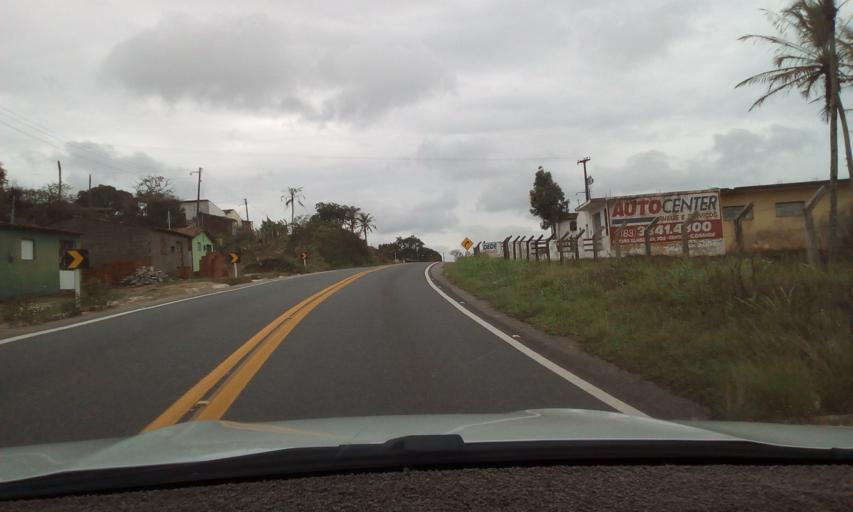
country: BR
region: Paraiba
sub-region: Areia
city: Remigio
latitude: -6.9618
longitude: -35.8029
